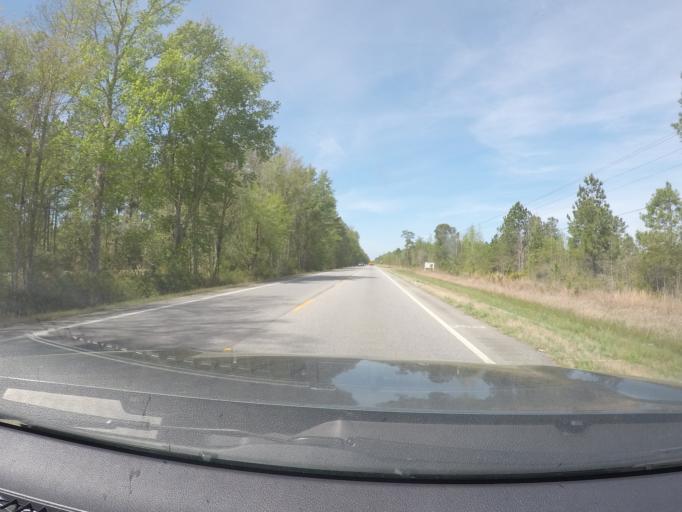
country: US
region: Georgia
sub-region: Bryan County
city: Pembroke
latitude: 32.1329
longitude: -81.5809
